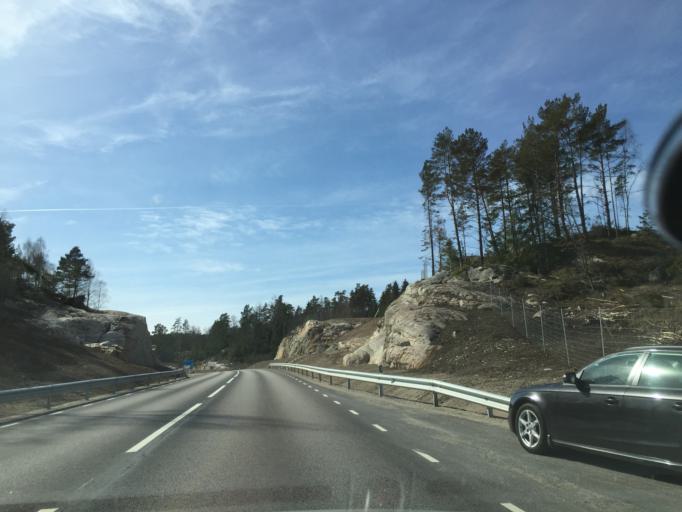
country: SE
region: Vaestra Goetaland
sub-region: Uddevalla Kommun
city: Uddevalla
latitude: 58.3550
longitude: 11.8065
